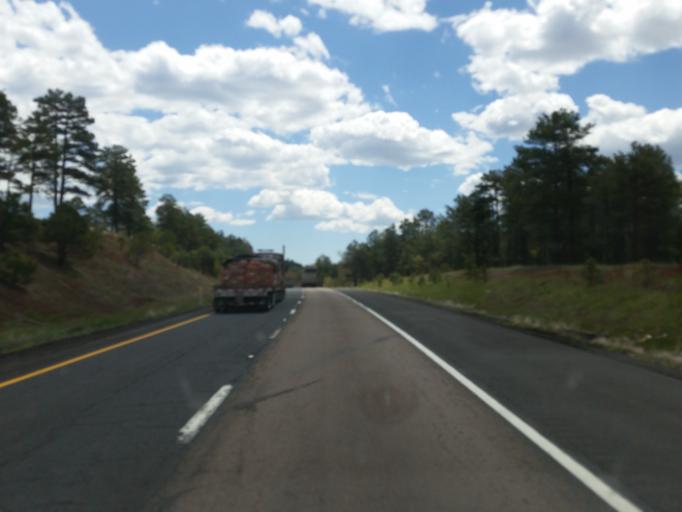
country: US
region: Arizona
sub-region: Coconino County
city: Parks
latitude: 35.2530
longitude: -111.9117
